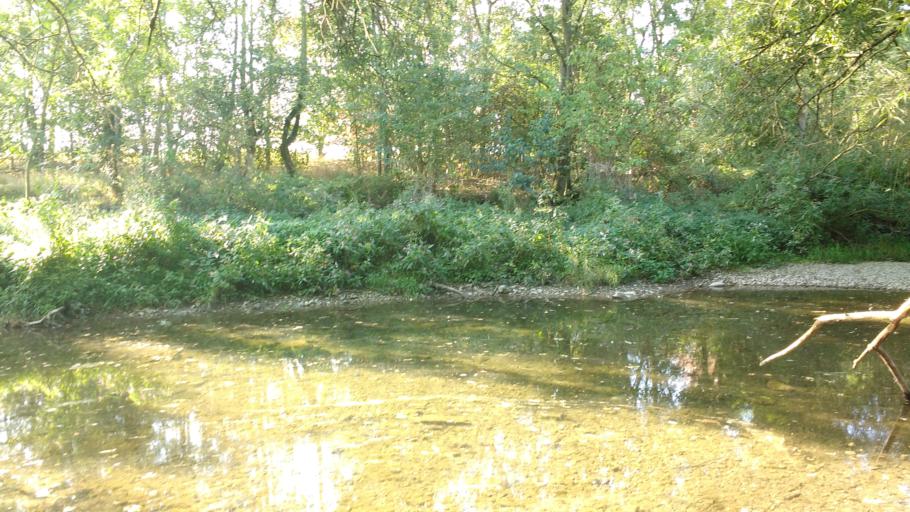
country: DE
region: North Rhine-Westphalia
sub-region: Regierungsbezirk Detmold
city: Paderborn
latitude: 51.7237
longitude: 8.7132
